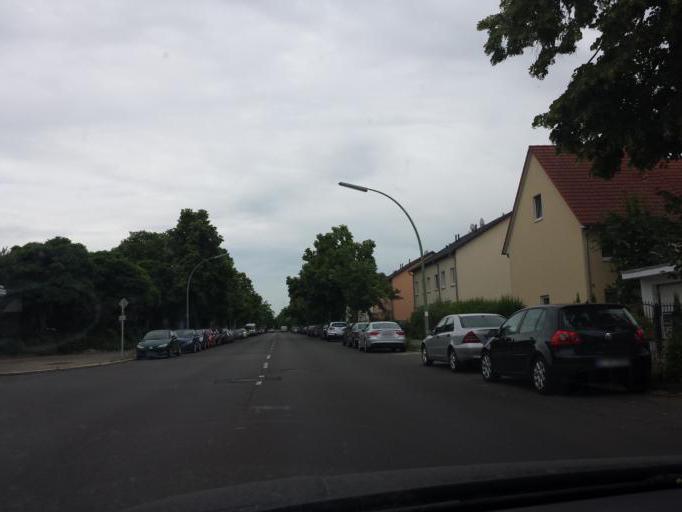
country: DE
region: Berlin
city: Marienfelde
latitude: 52.4127
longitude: 13.3779
